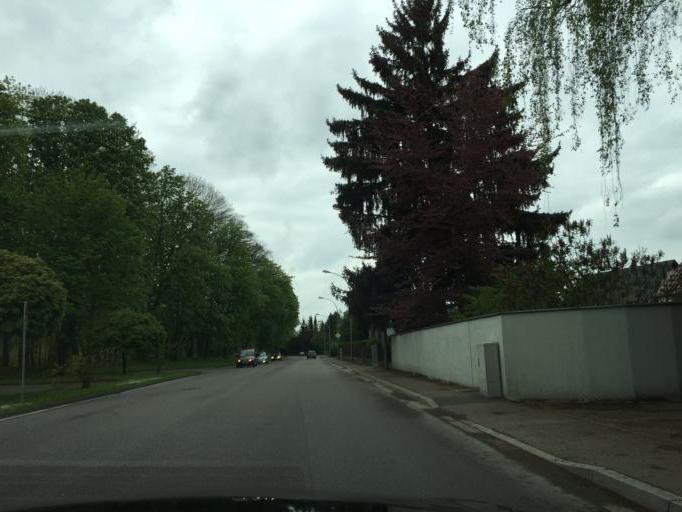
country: DE
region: Bavaria
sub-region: Swabia
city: Dillingen an der Donau
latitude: 48.5713
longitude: 10.4943
